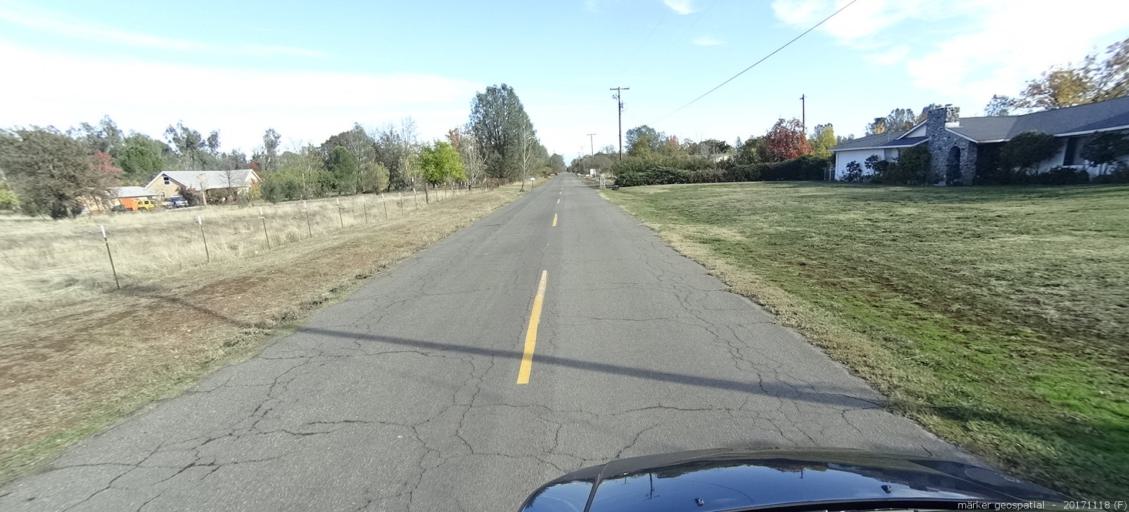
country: US
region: California
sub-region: Shasta County
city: Redding
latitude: 40.4690
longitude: -122.4200
